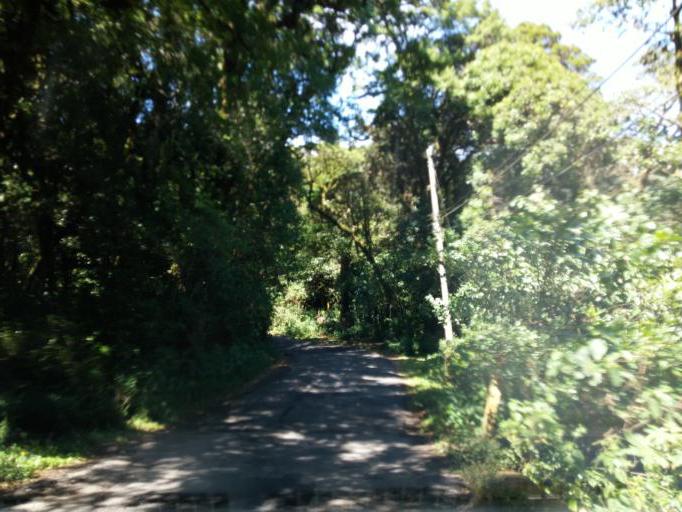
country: CR
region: Heredia
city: Santo Domingo
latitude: 10.0917
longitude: -84.1079
